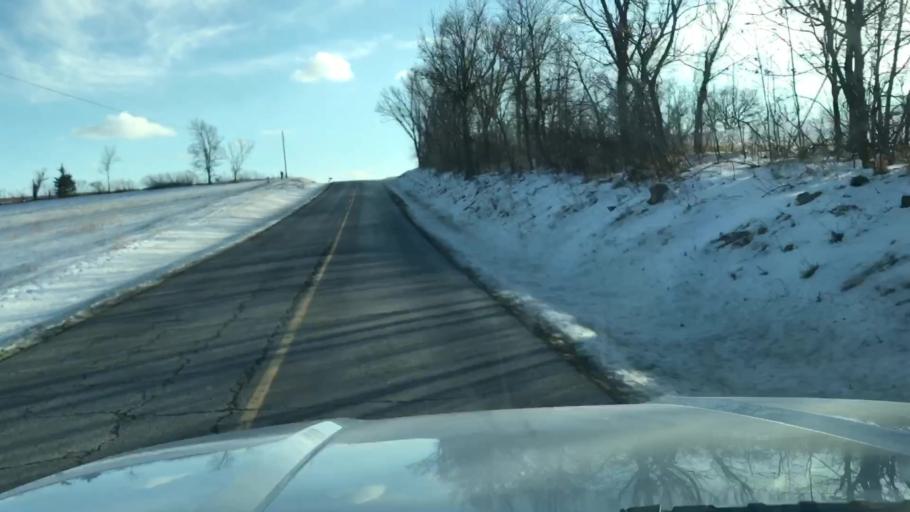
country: US
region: Missouri
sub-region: Holt County
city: Oregon
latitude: 40.0655
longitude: -94.9748
